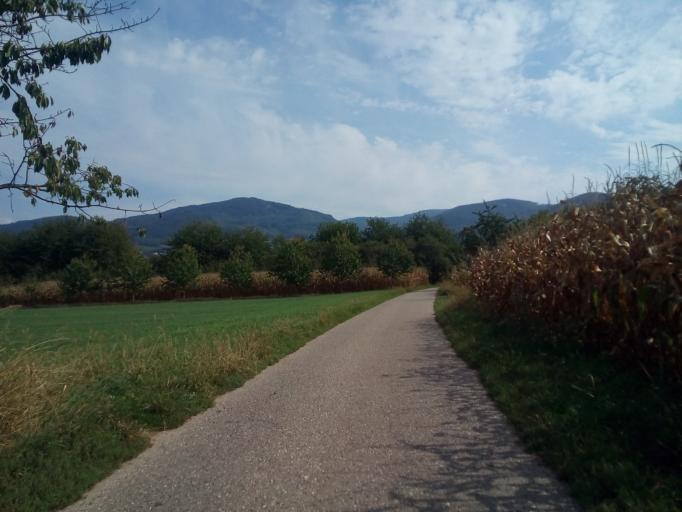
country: DE
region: Baden-Wuerttemberg
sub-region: Freiburg Region
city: Sasbach
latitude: 48.6492
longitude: 8.1085
